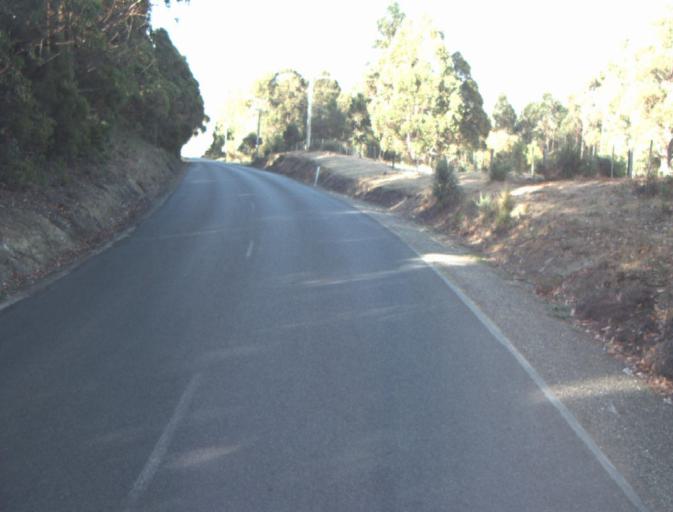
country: AU
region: Tasmania
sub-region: Launceston
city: Mayfield
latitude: -41.2155
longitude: 147.2101
